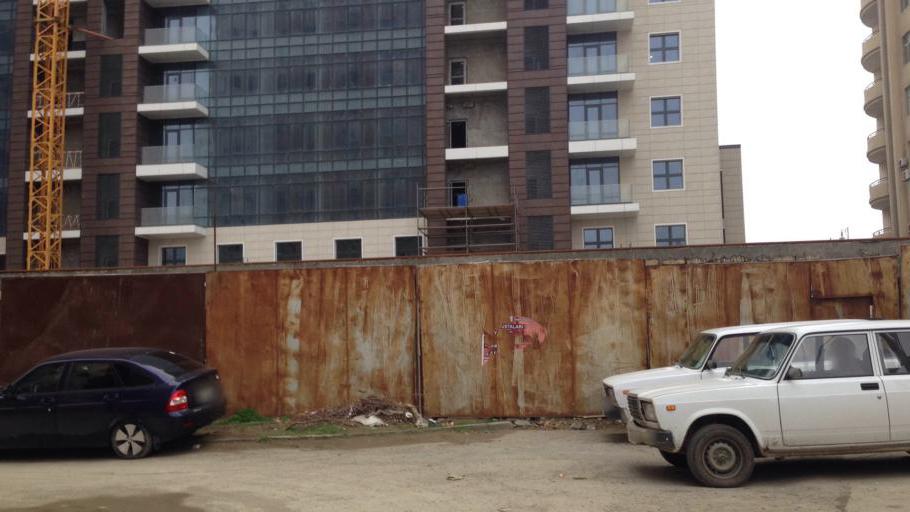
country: AZ
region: Baki
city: Baku
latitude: 40.3880
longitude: 49.8694
